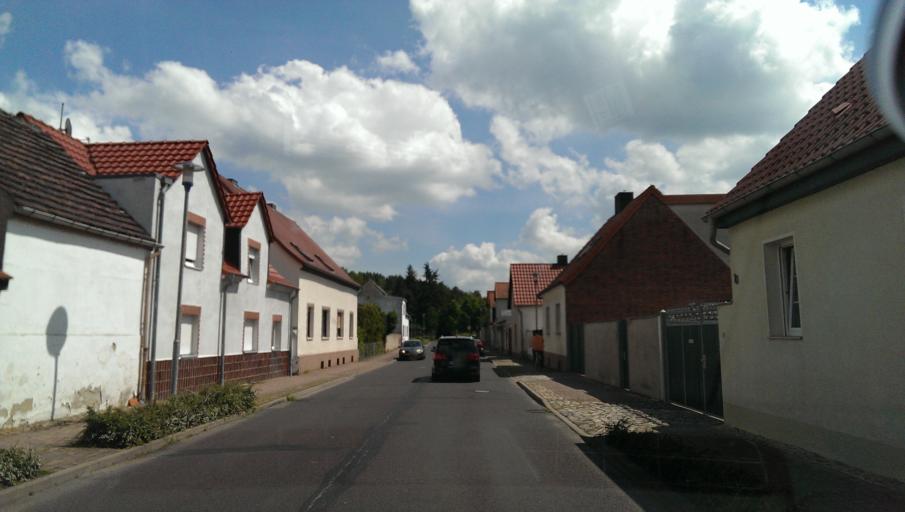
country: DE
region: Saxony-Anhalt
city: Plotzky
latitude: 52.0508
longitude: 11.8045
